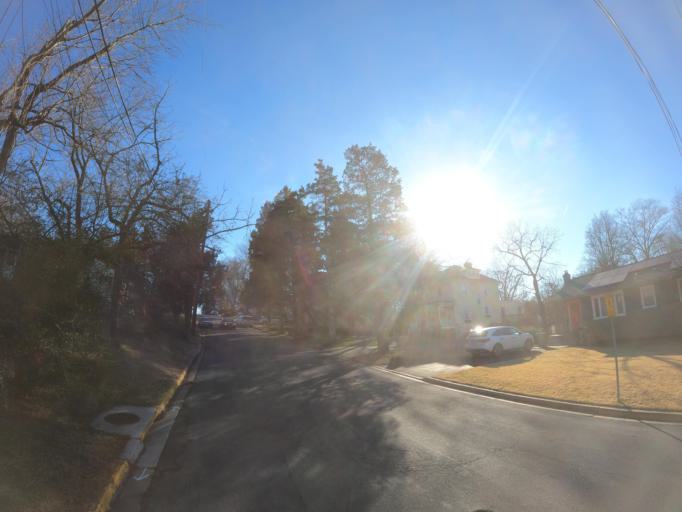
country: US
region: Maryland
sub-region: Prince George's County
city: Berwyn Heights
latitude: 38.9894
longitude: -76.9147
